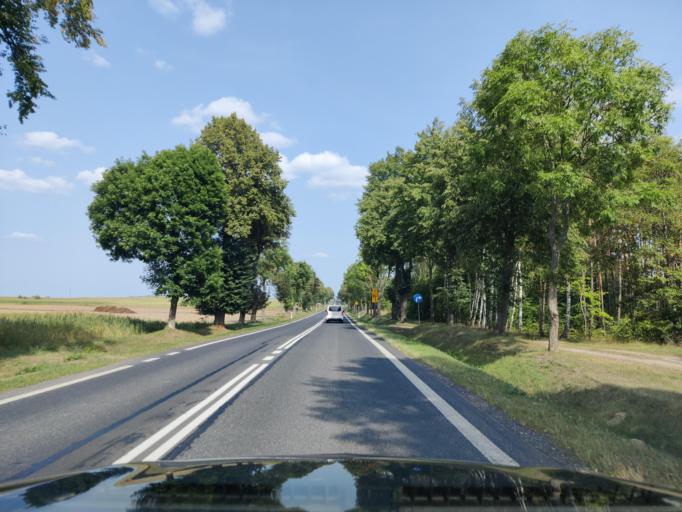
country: PL
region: Masovian Voivodeship
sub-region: Powiat makowski
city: Rzewnie
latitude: 52.8710
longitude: 21.3447
